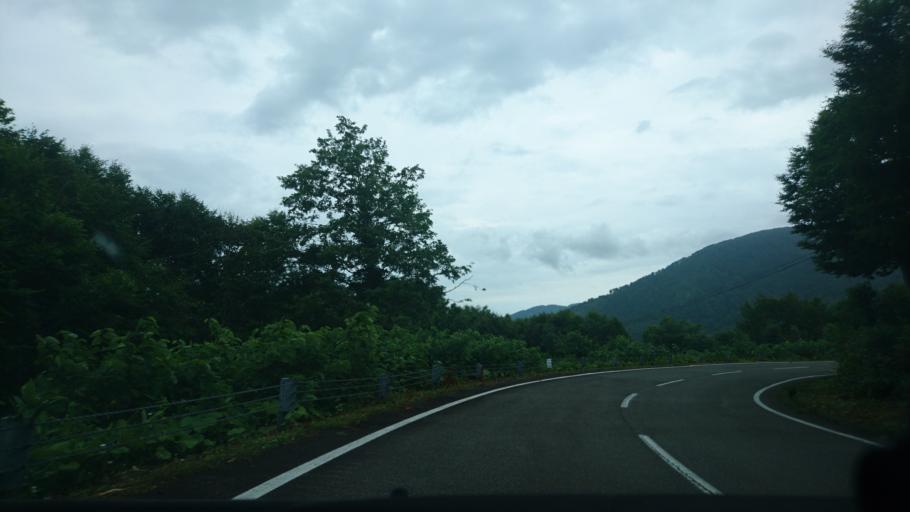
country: JP
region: Akita
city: Yuzawa
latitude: 39.1534
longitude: 140.7550
